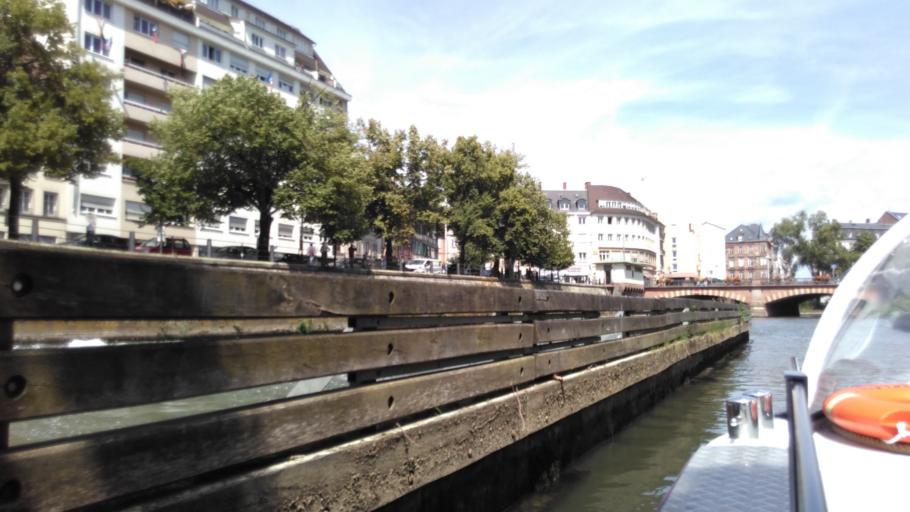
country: FR
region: Alsace
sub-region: Departement du Bas-Rhin
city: Strasbourg
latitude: 48.5815
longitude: 7.7384
